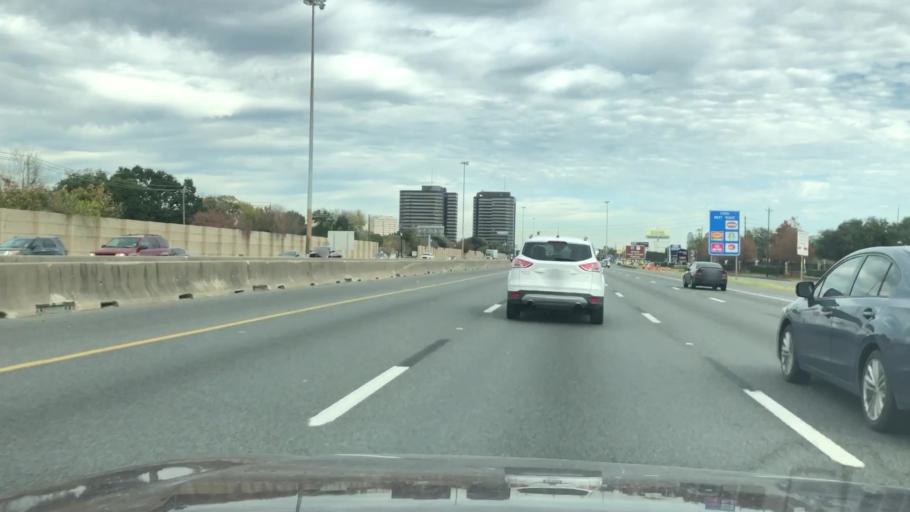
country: US
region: Texas
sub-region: Harris County
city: Piney Point Village
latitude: 29.6950
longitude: -95.5235
